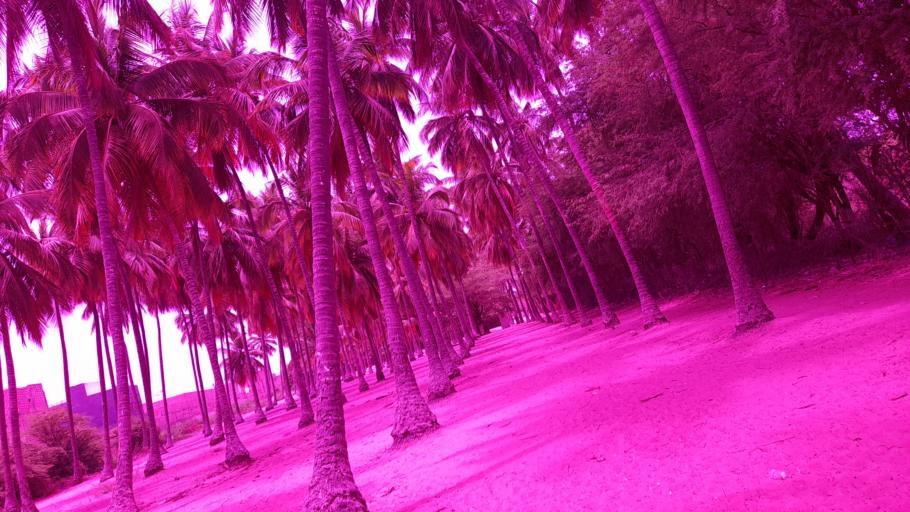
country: SN
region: Saint-Louis
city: Saint-Louis
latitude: 16.0153
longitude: -16.4872
